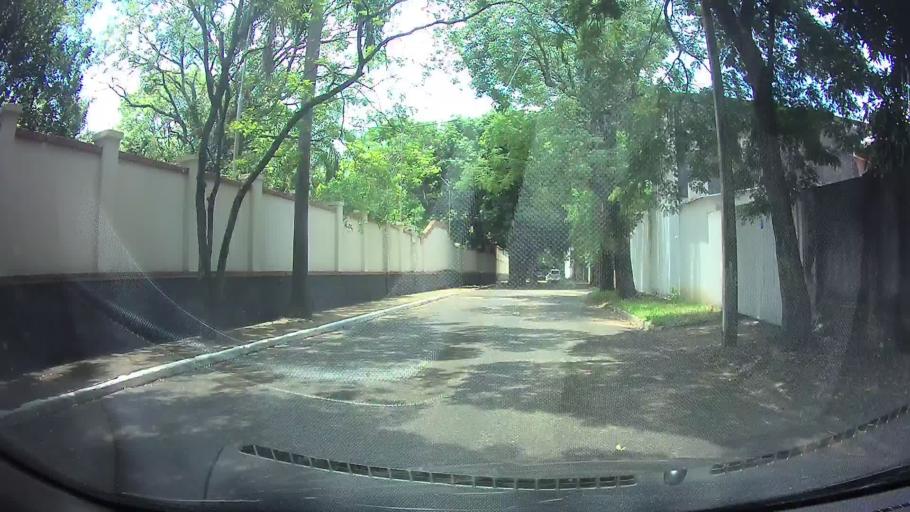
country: PY
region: Asuncion
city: Asuncion
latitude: -25.2942
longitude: -57.6010
